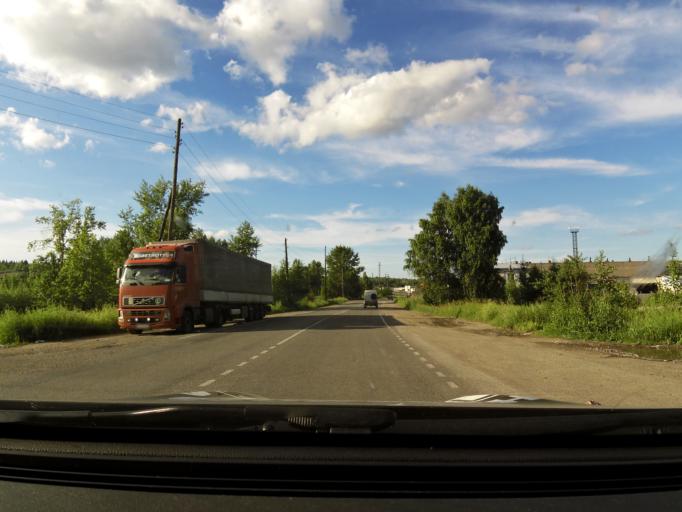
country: RU
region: Kirov
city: Omutninsk
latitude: 58.6924
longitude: 52.2173
